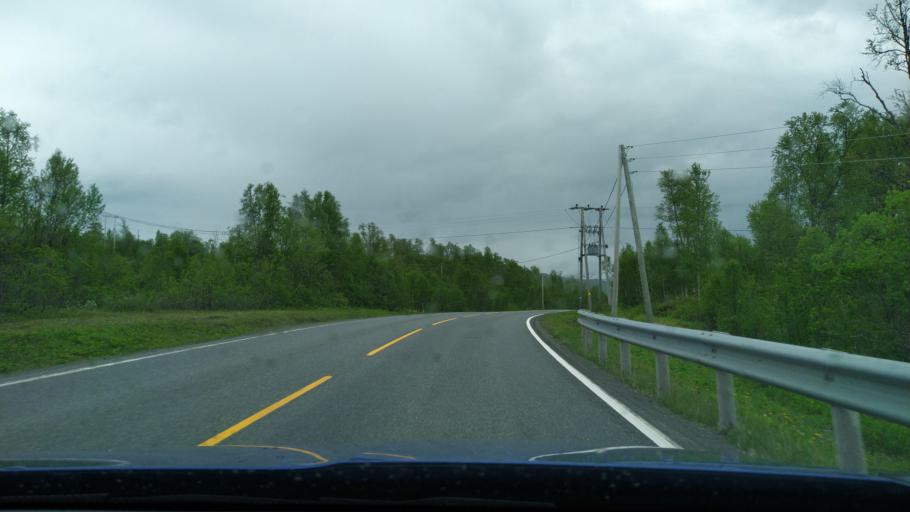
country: NO
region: Troms
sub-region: Balsfjord
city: Storsteinnes
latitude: 69.1272
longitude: 18.9905
